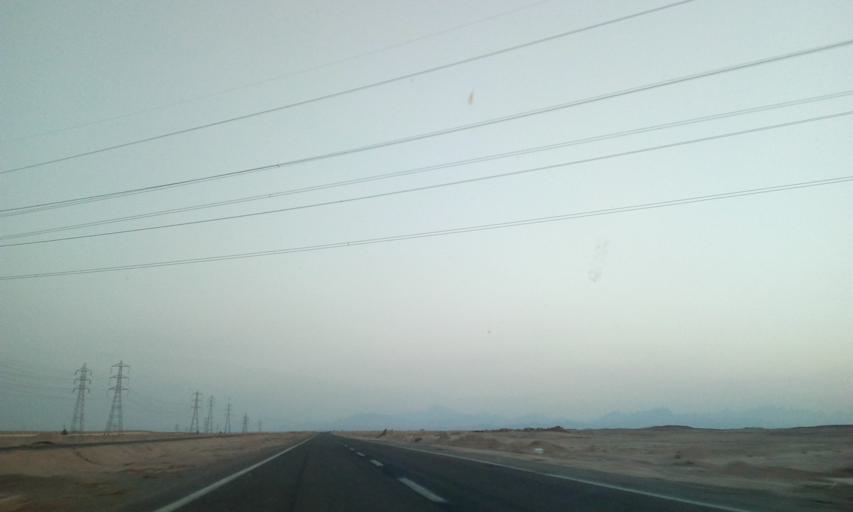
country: EG
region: Red Sea
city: El Gouna
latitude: 27.3245
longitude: 33.6652
